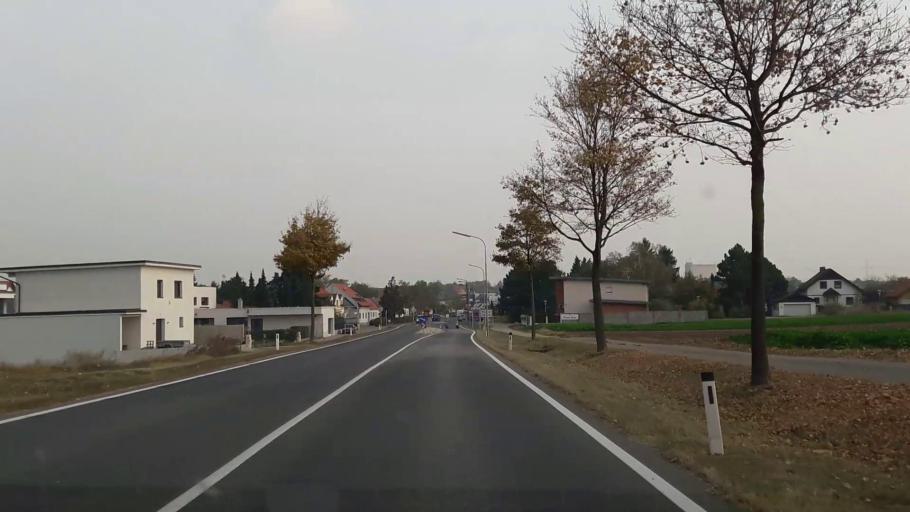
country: AT
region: Burgenland
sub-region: Politischer Bezirk Neusiedl am See
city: Parndorf
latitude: 47.9990
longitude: 16.8493
